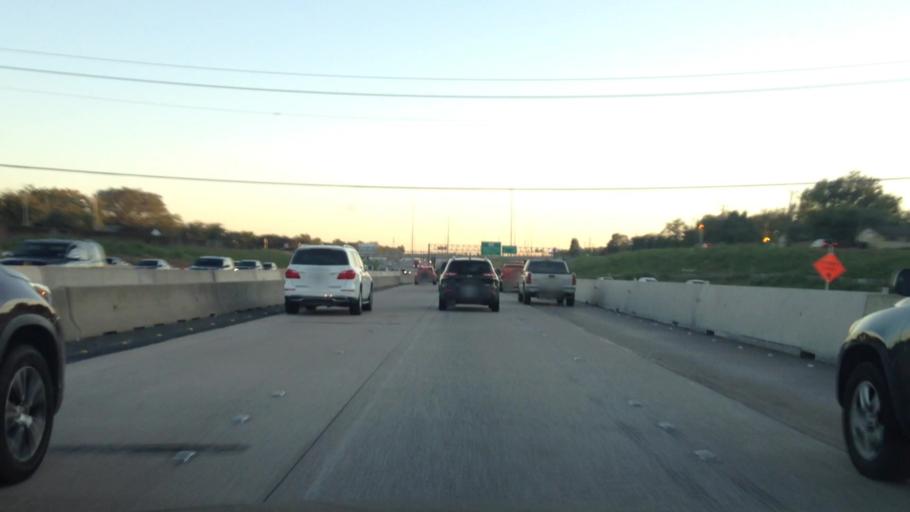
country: US
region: Texas
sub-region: Tarrant County
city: Arlington
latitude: 32.7285
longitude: -97.0623
